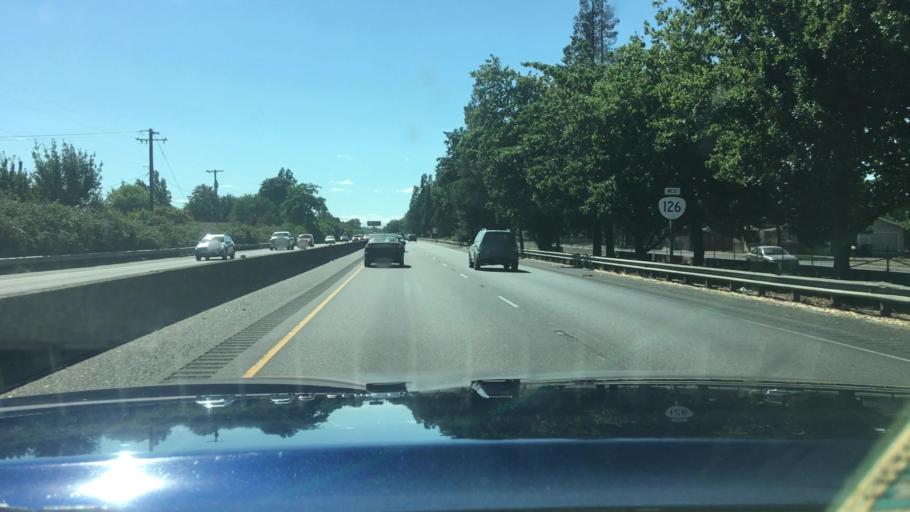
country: US
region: Oregon
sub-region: Lane County
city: Springfield
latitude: 44.0622
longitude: -123.0041
